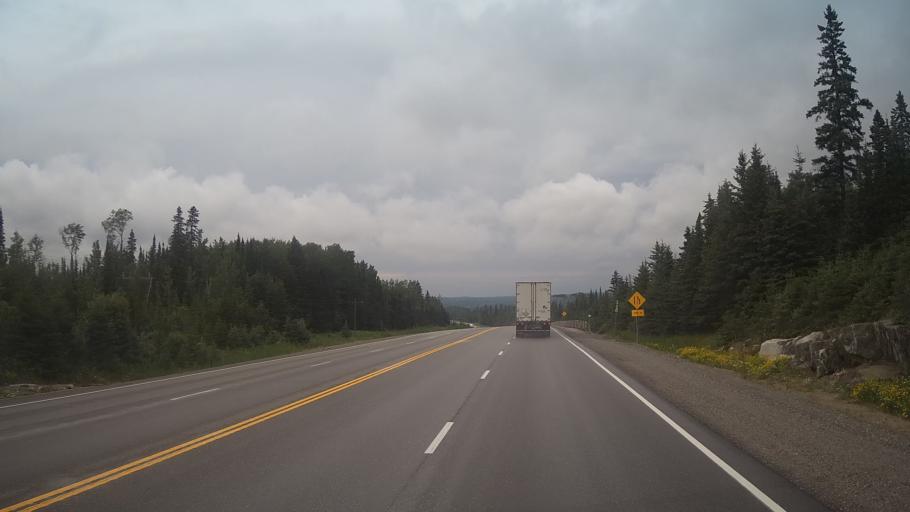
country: CA
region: Ontario
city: Neebing
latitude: 48.7002
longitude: -89.8905
